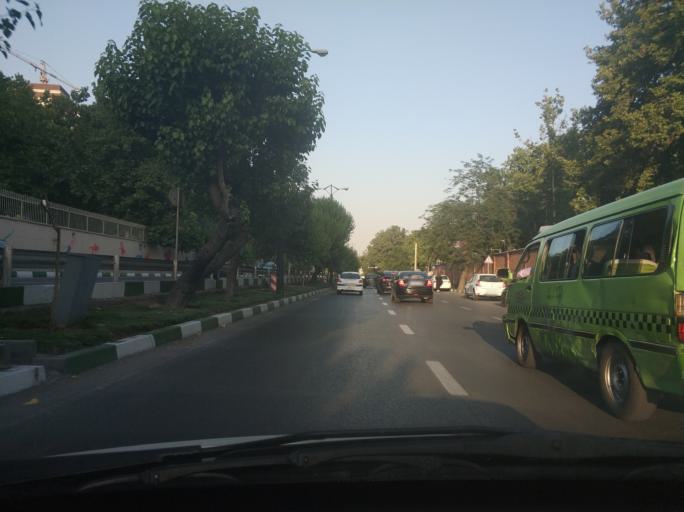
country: IR
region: Tehran
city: Tajrish
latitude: 35.8009
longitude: 51.4632
